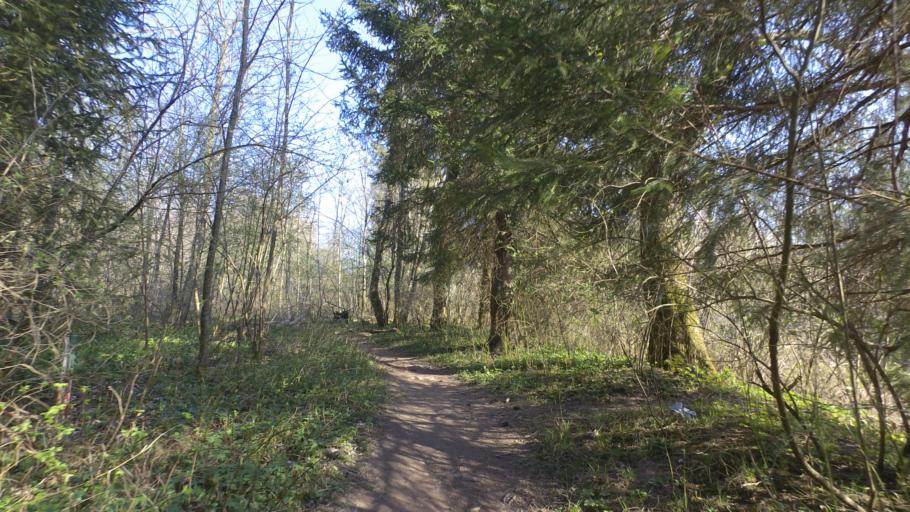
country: DE
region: Bavaria
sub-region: Upper Bavaria
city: Traunreut
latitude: 47.9578
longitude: 12.5808
